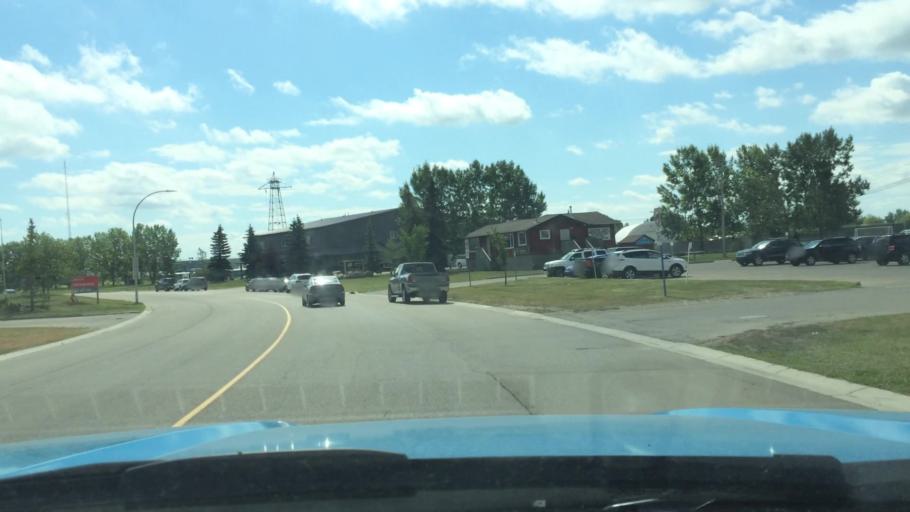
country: CA
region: Alberta
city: Airdrie
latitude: 51.2893
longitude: -113.9912
